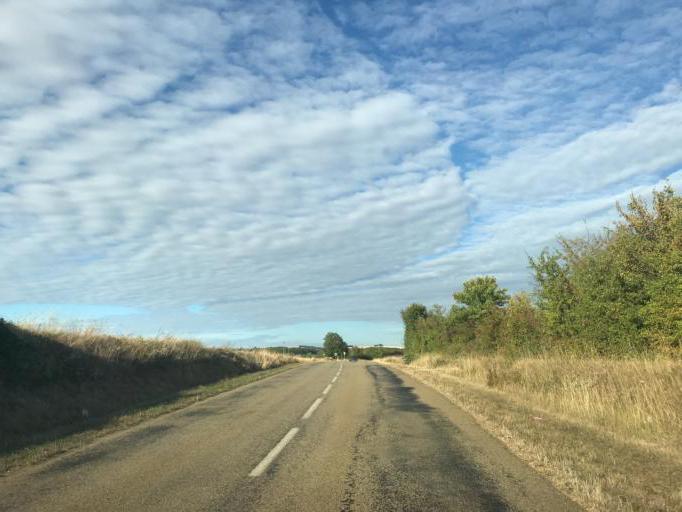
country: FR
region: Bourgogne
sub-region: Departement de l'Yonne
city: Fontenailles
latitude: 47.6073
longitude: 3.4896
